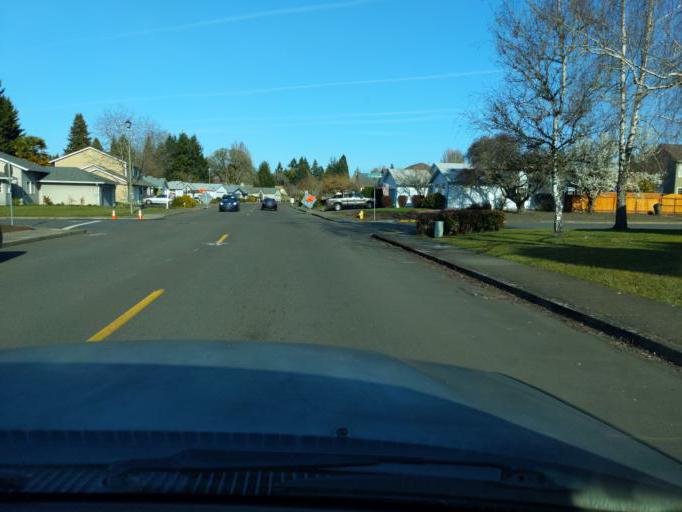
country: US
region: Oregon
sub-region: Yamhill County
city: McMinnville
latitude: 45.2019
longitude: -123.2146
